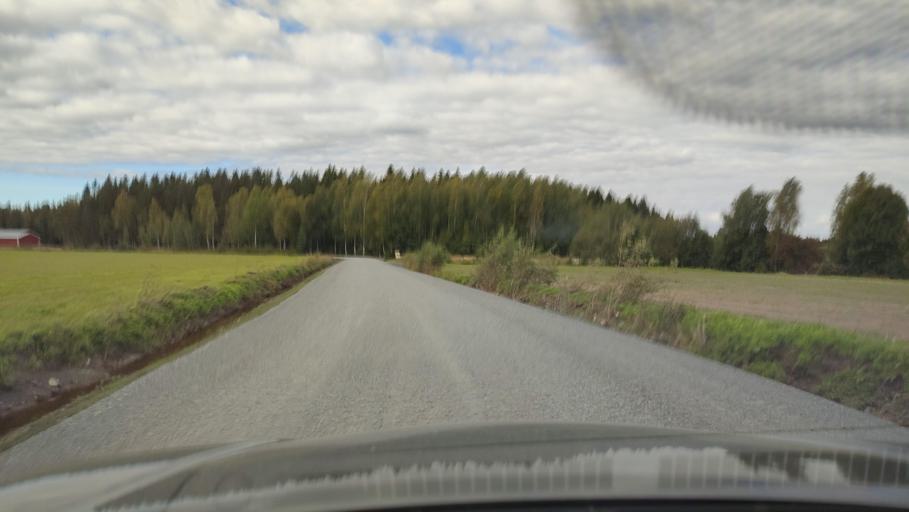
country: FI
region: Southern Ostrobothnia
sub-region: Suupohja
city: Karijoki
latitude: 62.2314
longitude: 21.6165
